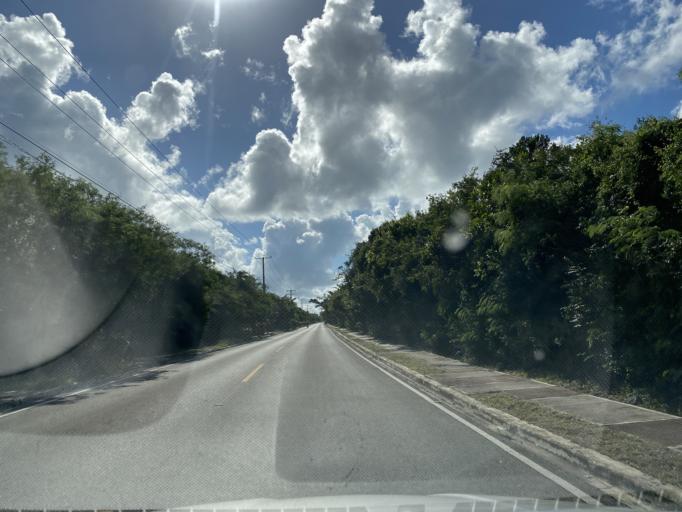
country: DO
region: La Altagracia
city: San Rafael del Yuma
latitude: 18.3410
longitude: -68.8126
